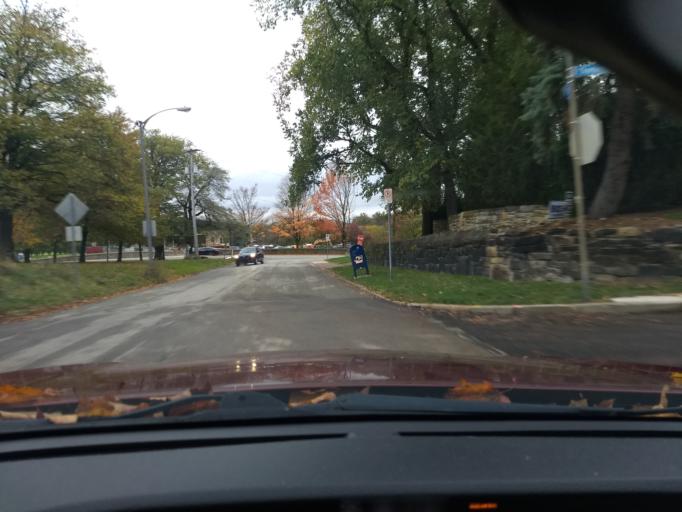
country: US
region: Pennsylvania
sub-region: Allegheny County
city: Bloomfield
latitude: 40.4370
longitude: -79.9339
